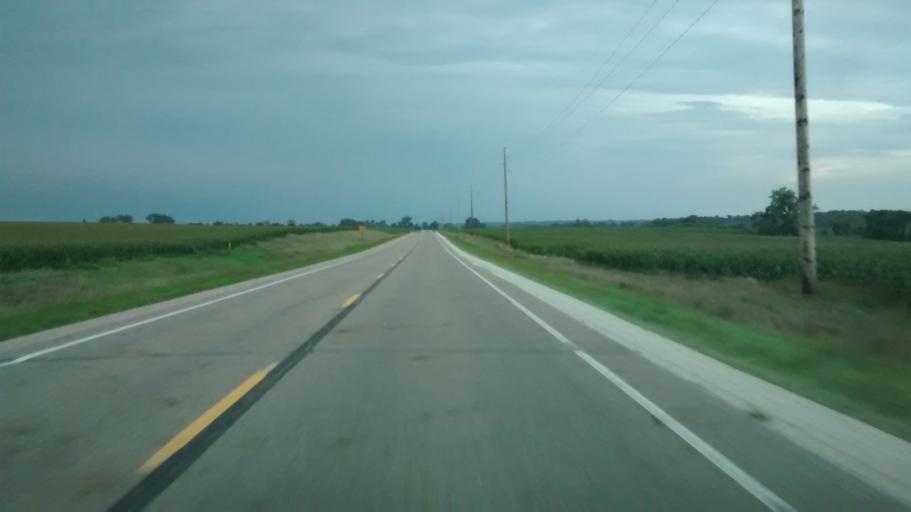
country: US
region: Iowa
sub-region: Plymouth County
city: Kingsley
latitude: 42.5702
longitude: -95.9989
